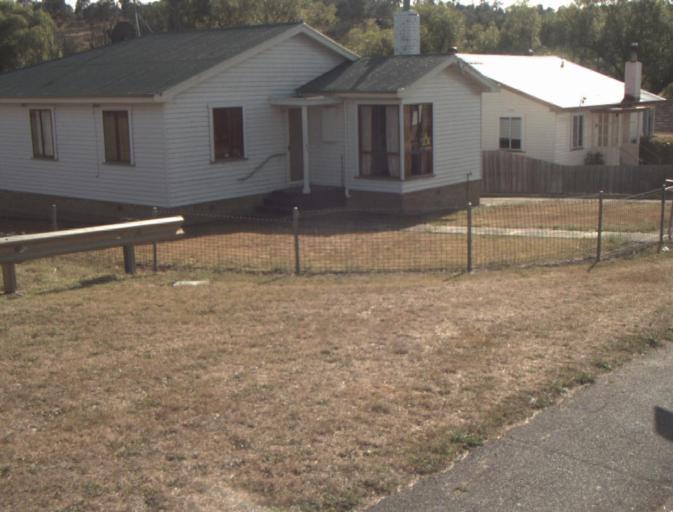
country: AU
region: Tasmania
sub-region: Launceston
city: Mayfield
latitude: -41.3858
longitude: 147.1330
